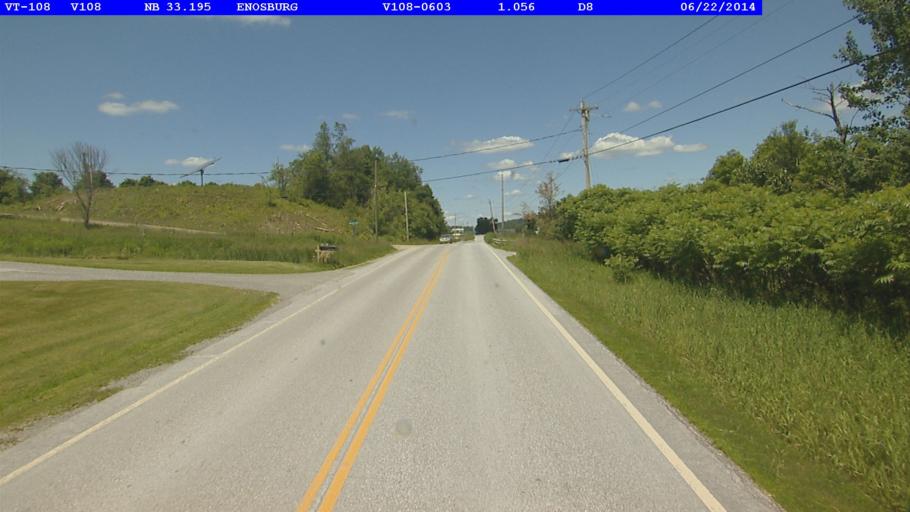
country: US
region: Vermont
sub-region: Franklin County
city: Enosburg Falls
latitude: 44.8532
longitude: -72.8038
